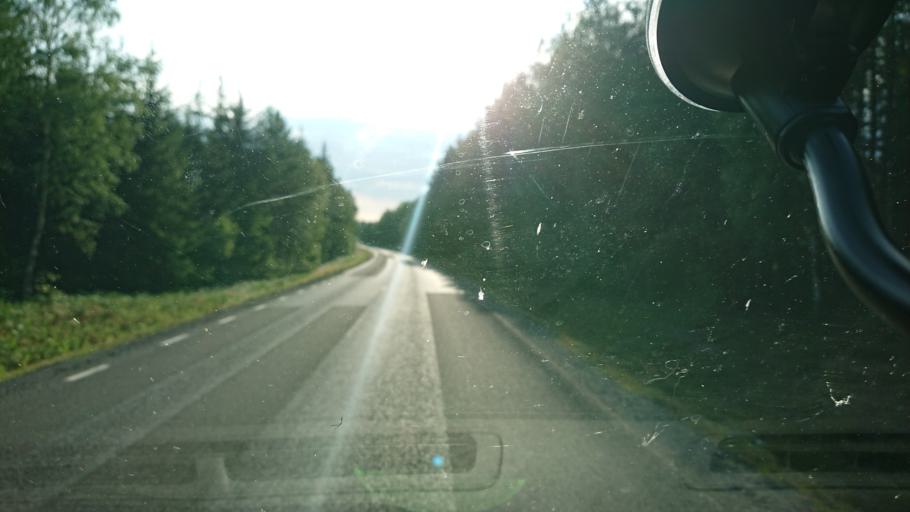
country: SE
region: Kronoberg
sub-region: Vaxjo Kommun
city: Rottne
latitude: 57.0332
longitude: 14.9589
